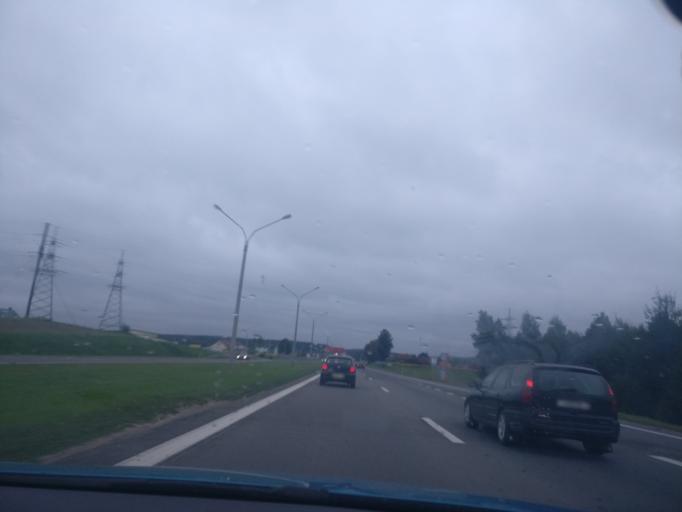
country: BY
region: Minsk
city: Korolev Stan
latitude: 53.9923
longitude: 27.8083
